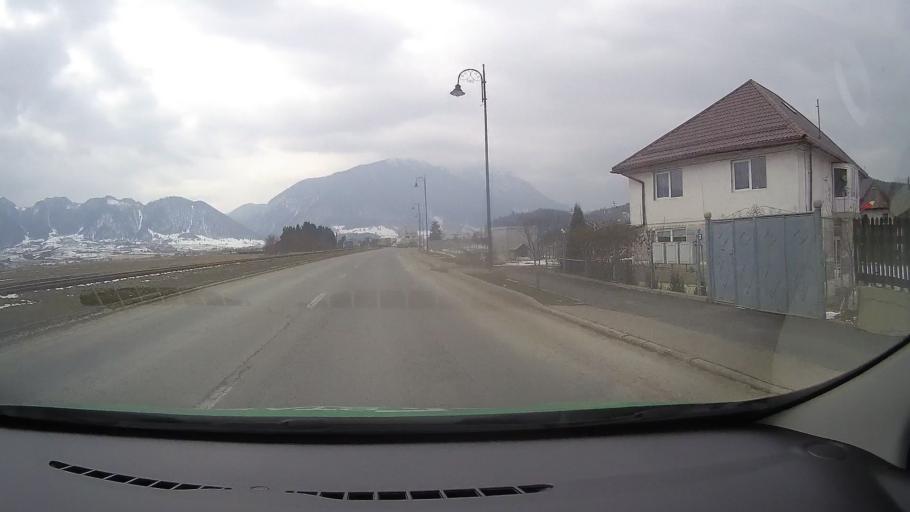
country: RO
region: Brasov
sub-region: Comuna Zarnesti
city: Zarnesti
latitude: 45.5669
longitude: 25.3438
